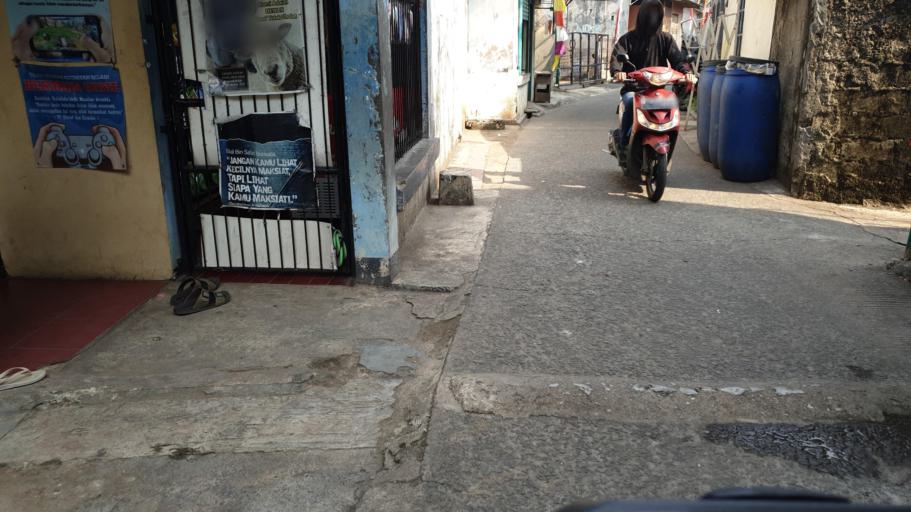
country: ID
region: West Java
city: Depok
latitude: -6.3716
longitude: 106.8552
